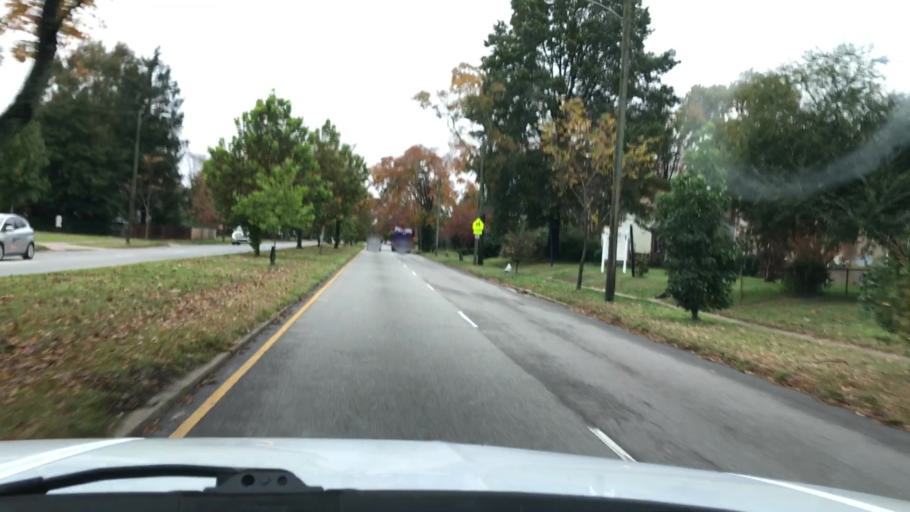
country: US
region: Virginia
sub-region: Henrico County
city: Lakeside
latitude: 37.5927
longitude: -77.4487
